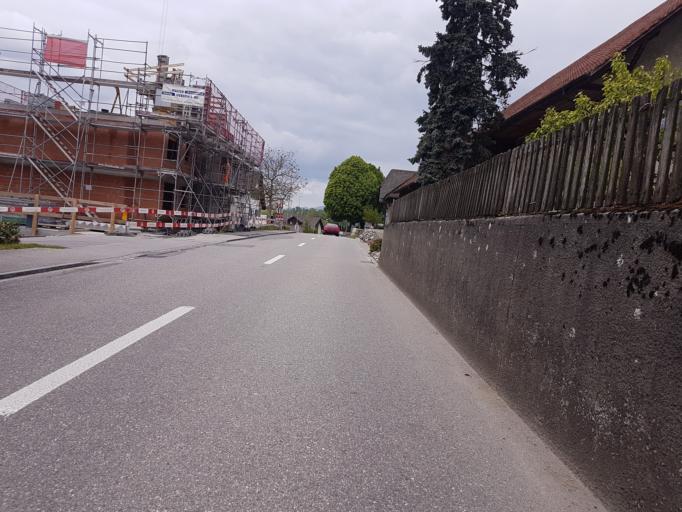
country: CH
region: Bern
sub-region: Oberaargau
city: Oberbipp
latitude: 47.2359
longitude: 7.6904
